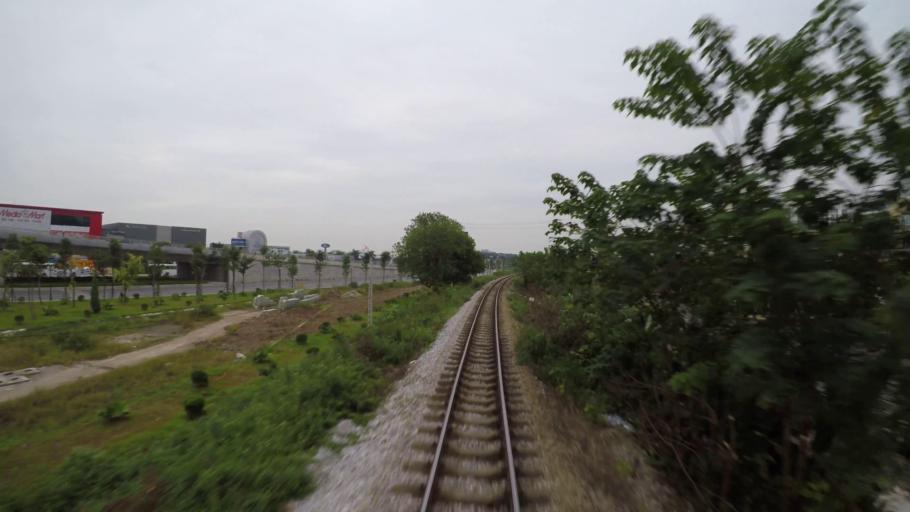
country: VN
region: Ha Noi
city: Trau Quy
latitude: 21.0177
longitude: 105.9429
